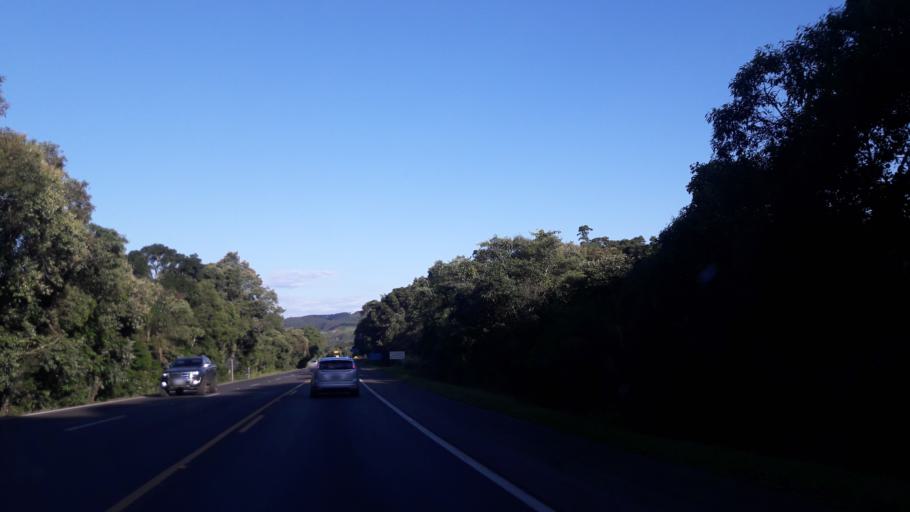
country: BR
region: Parana
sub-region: Prudentopolis
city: Prudentopolis
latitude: -25.3122
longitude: -51.1828
